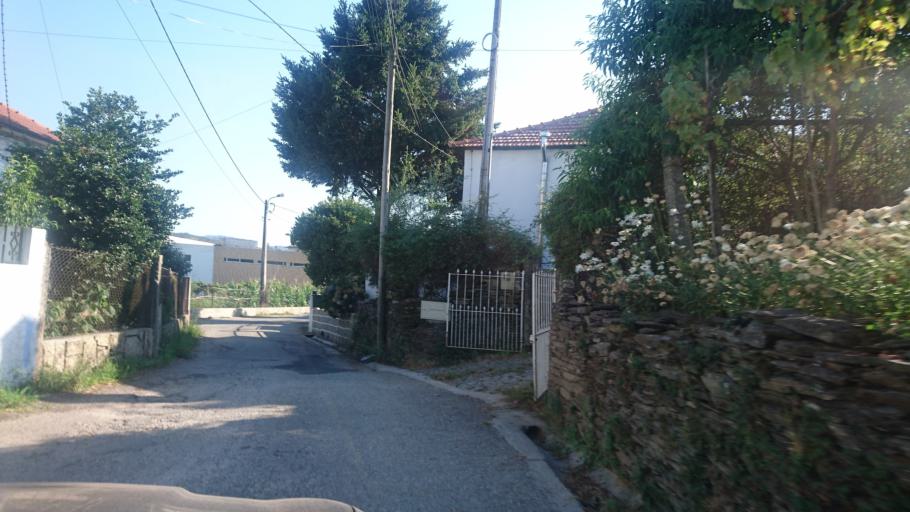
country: PT
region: Porto
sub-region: Paredes
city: Recarei
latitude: 41.1542
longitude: -8.4048
